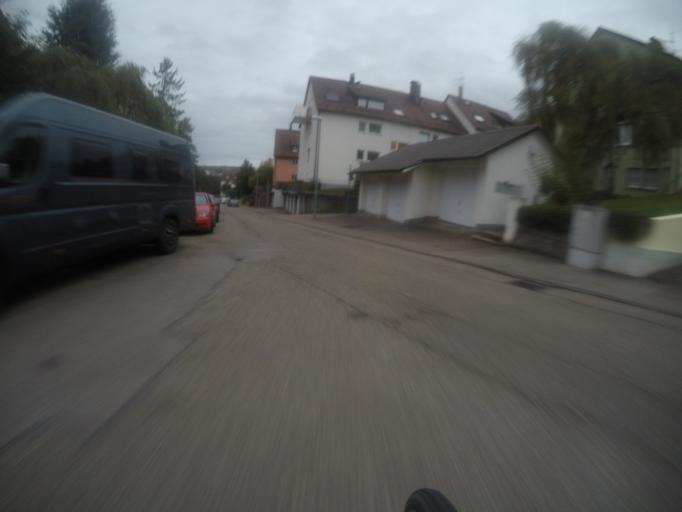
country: DE
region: Baden-Wuerttemberg
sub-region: Regierungsbezirk Stuttgart
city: Stuttgart-Ost
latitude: 48.7752
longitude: 9.2352
